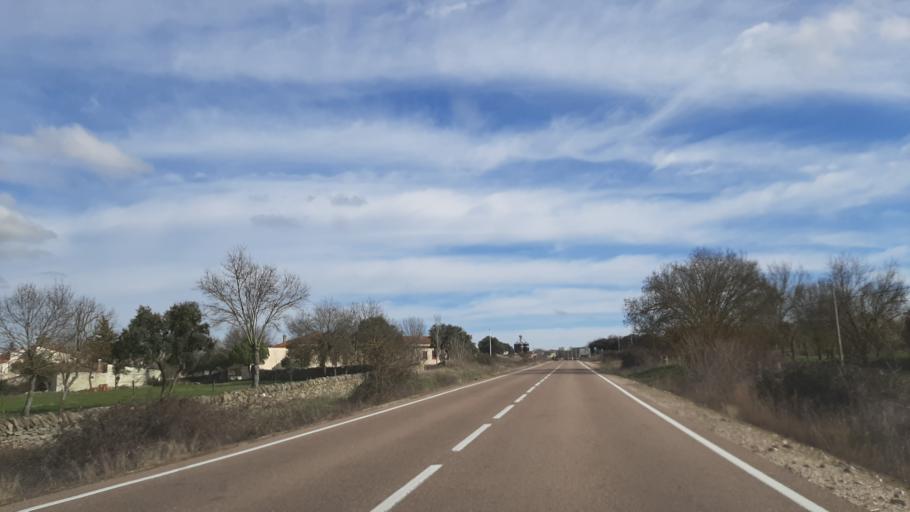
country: ES
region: Castille and Leon
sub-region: Provincia de Salamanca
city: Monleras
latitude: 41.1852
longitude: -6.2314
